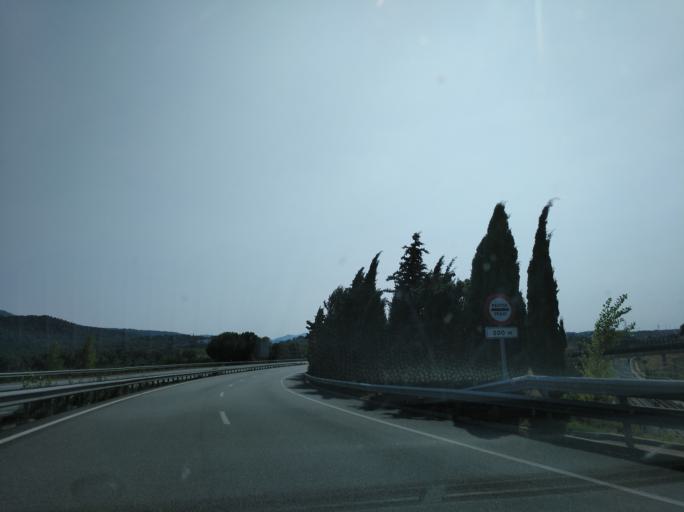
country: ES
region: Catalonia
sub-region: Provincia de Barcelona
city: La Roca del Valles
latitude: 41.6003
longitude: 2.3362
